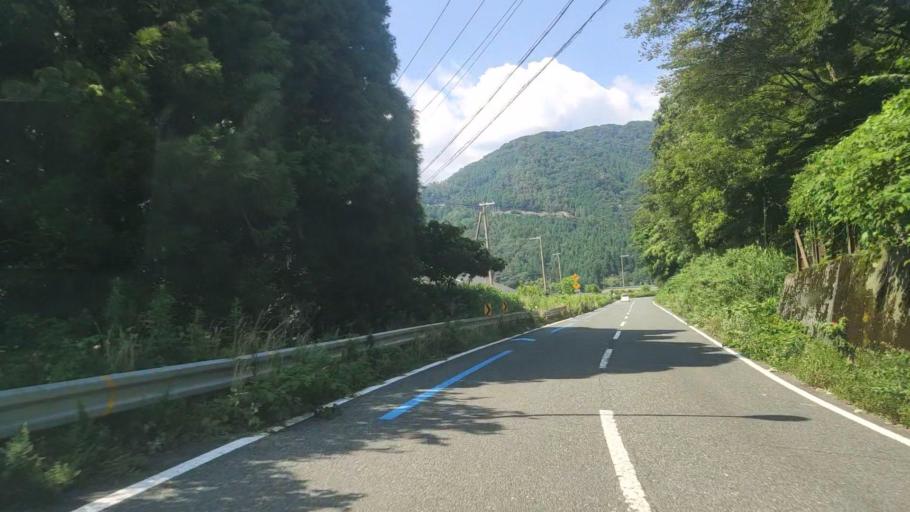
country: JP
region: Shiga Prefecture
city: Nagahama
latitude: 35.5099
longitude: 136.1686
